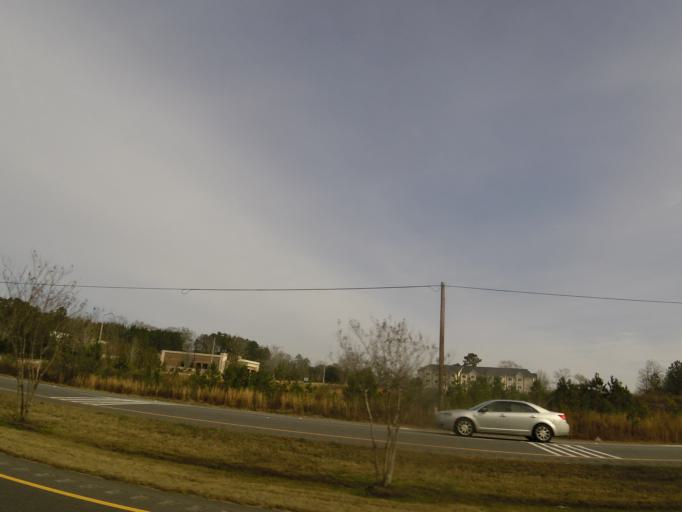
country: US
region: Alabama
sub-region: Dale County
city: Ozark
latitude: 31.4708
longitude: -85.6778
